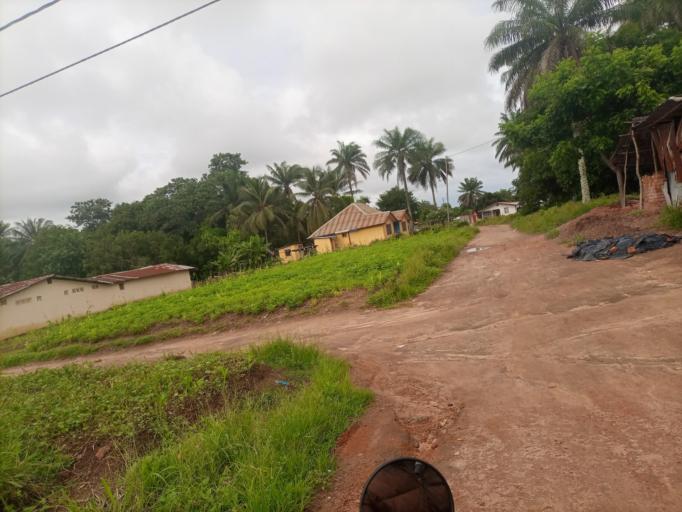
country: SL
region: Northern Province
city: Masoyila
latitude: 8.5968
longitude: -13.1710
